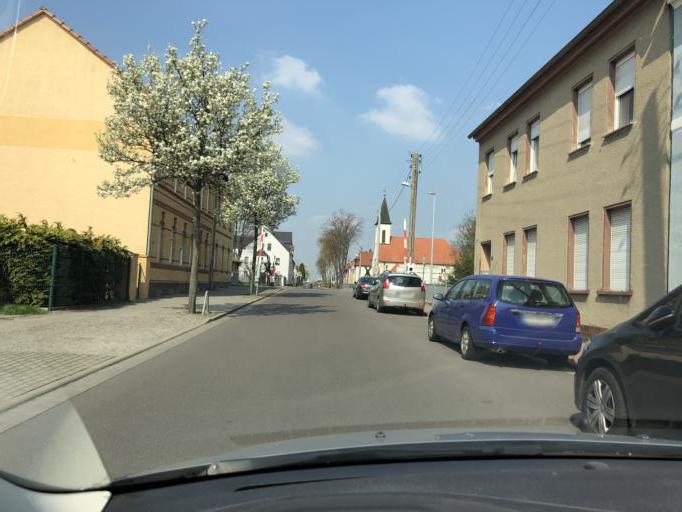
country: DE
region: Saxony-Anhalt
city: Zorbig
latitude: 51.6302
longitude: 12.1223
